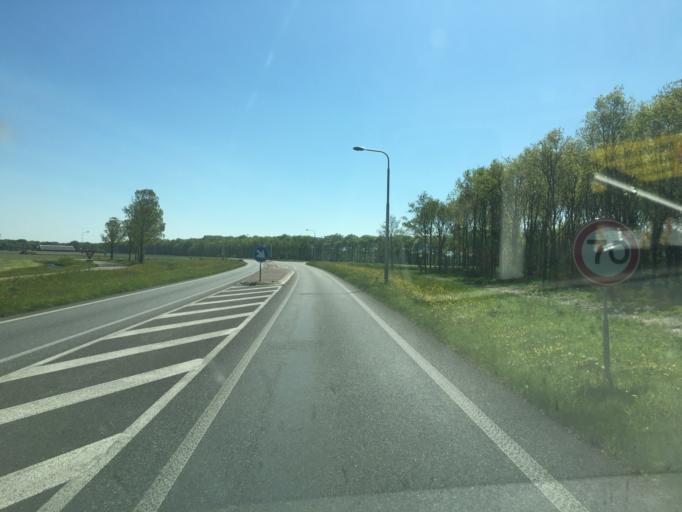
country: NL
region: Friesland
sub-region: Gemeente Gaasterlan-Sleat
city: Oudemirdum
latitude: 52.8753
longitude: 5.5134
